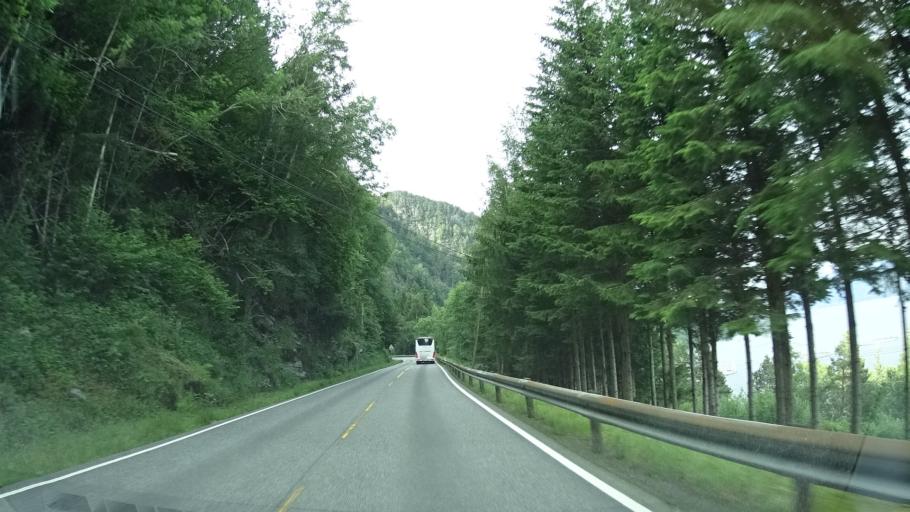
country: NO
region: Hordaland
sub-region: Kvam
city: Norheimsund
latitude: 60.3178
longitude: 6.1725
